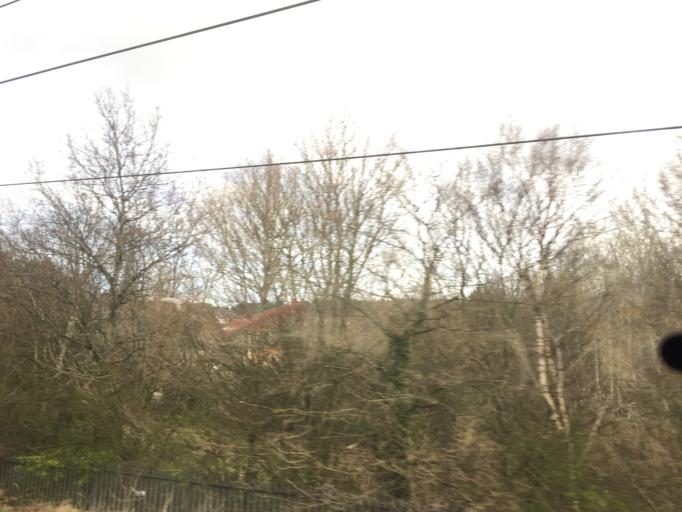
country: GB
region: England
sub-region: Cumbria
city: Penrith
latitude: 54.6665
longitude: -2.7594
